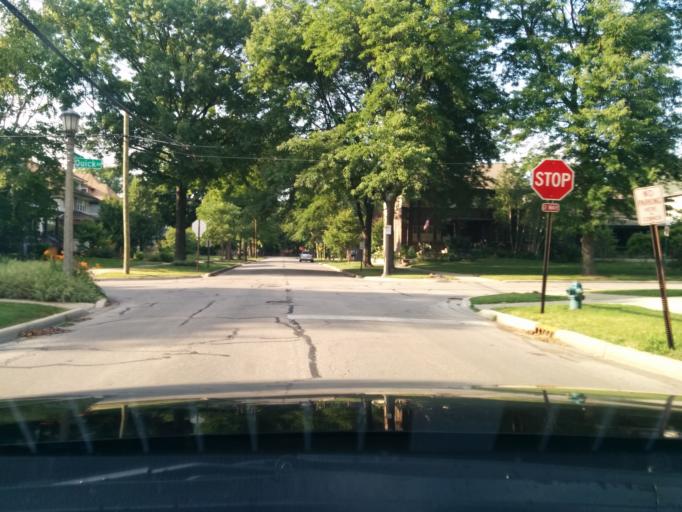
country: US
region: Illinois
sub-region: Cook County
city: River Forest
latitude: 41.8905
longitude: -87.8072
